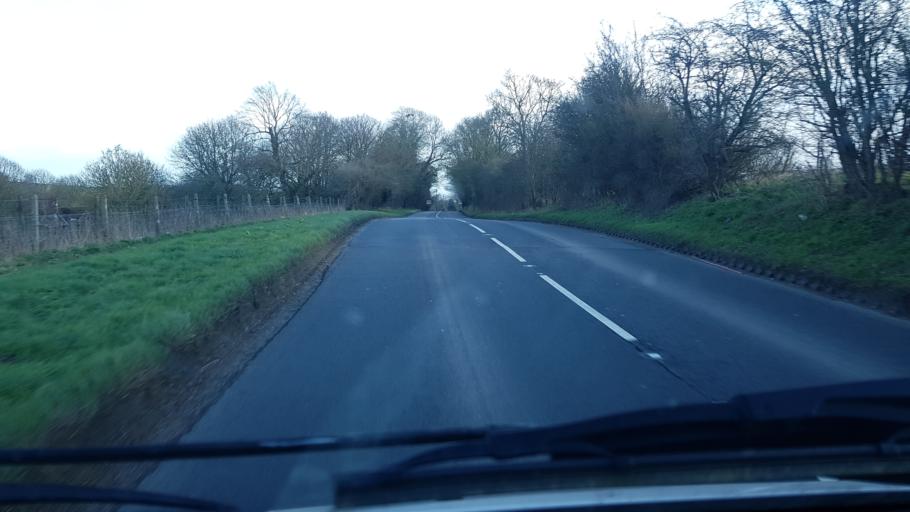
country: GB
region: England
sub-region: Wiltshire
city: Collingbourne Kingston
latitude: 51.2927
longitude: -1.6545
